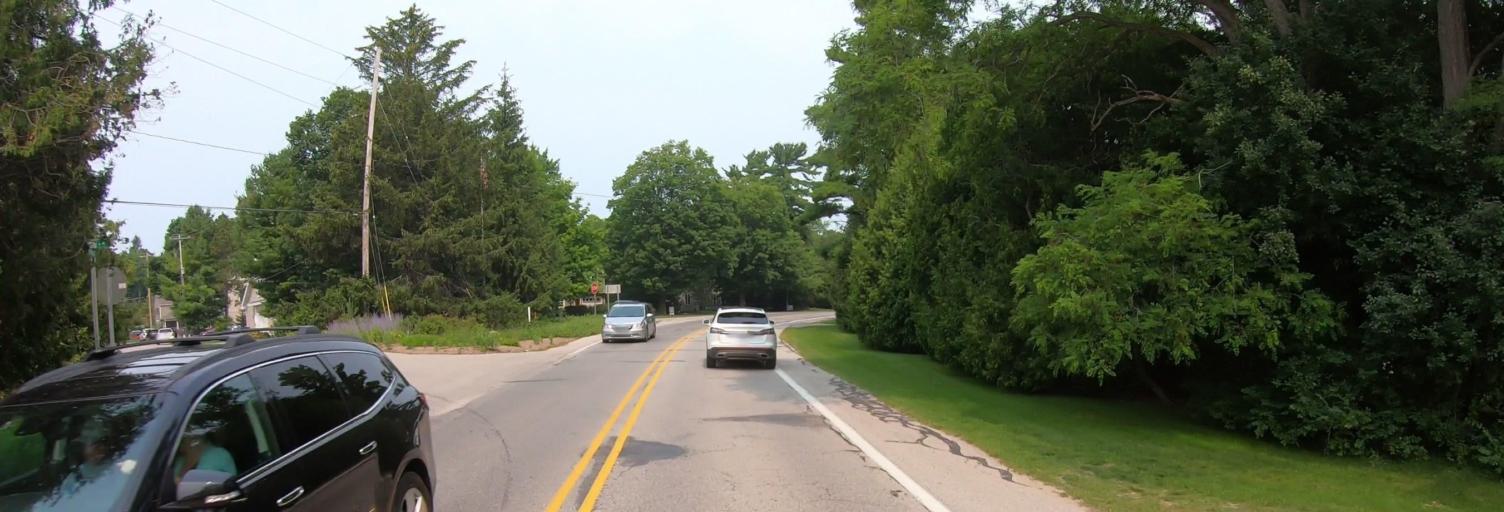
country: US
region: Michigan
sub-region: Leelanau County
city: Leland
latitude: 45.0180
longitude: -85.7622
